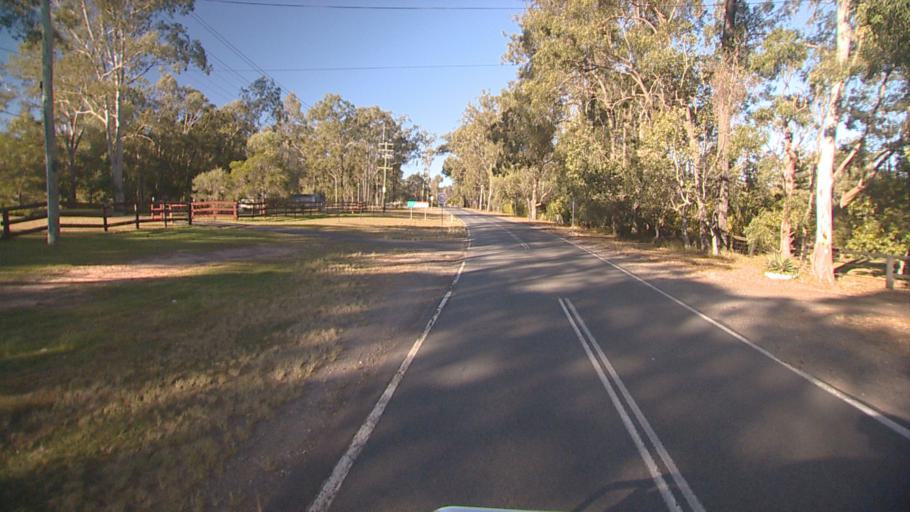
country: AU
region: Queensland
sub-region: Logan
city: North Maclean
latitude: -27.7580
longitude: 153.0265
